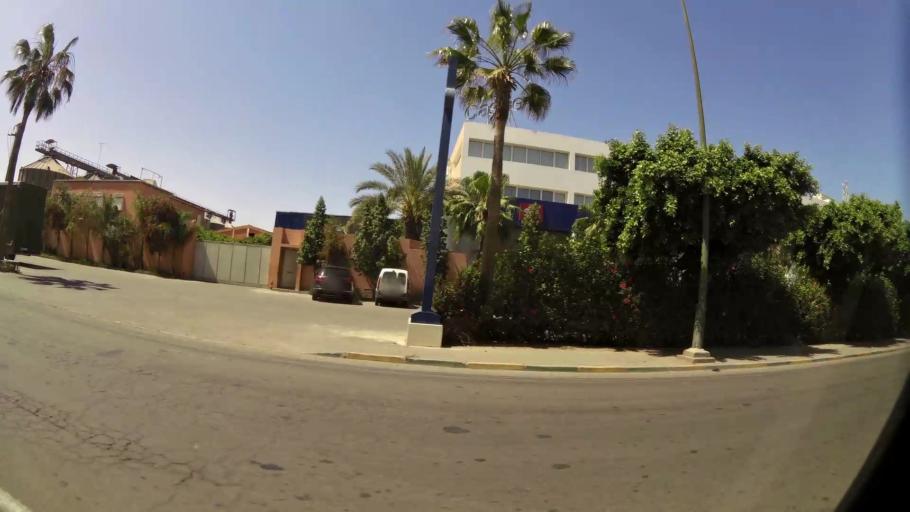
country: MA
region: Souss-Massa-Draa
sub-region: Inezgane-Ait Mellou
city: Inezgane
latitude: 30.3263
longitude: -9.4849
